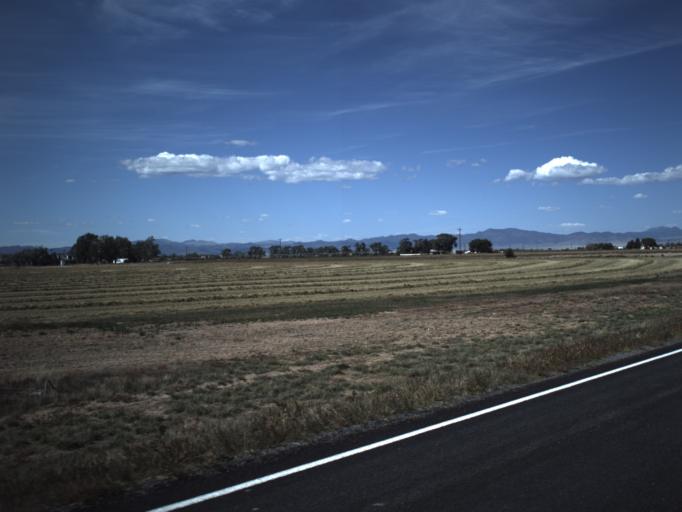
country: US
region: Utah
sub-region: Washington County
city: Enterprise
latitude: 37.6895
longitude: -113.6565
